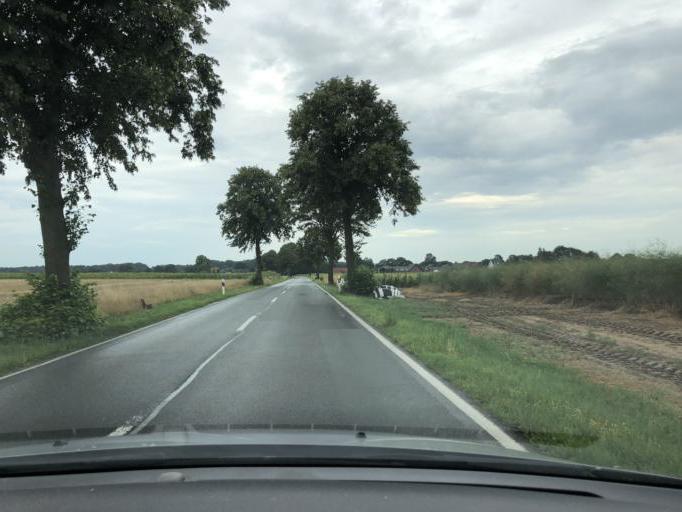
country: DE
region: North Rhine-Westphalia
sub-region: Regierungsbezirk Dusseldorf
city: Schermbeck
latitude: 51.6521
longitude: 6.8932
